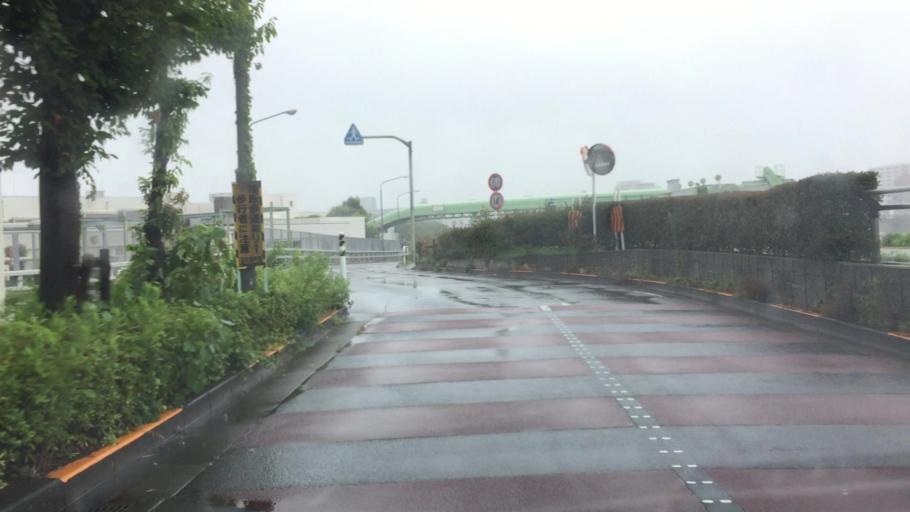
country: JP
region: Saitama
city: Soka
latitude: 35.7417
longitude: 139.7903
